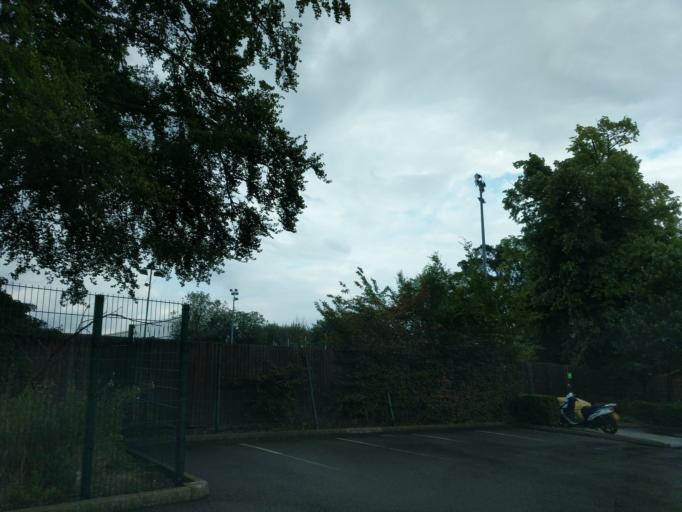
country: GB
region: England
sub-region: Suffolk
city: Lakenheath
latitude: 52.3421
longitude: 0.5141
